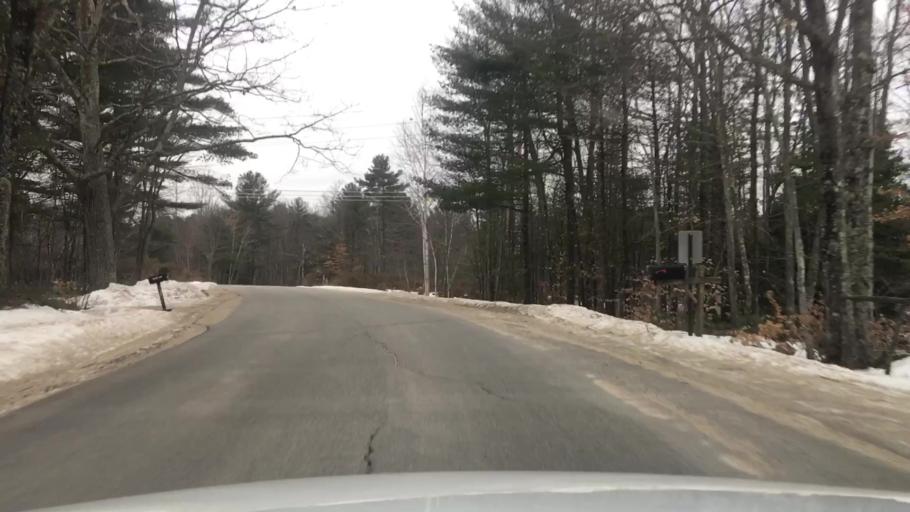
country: US
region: Maine
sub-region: York County
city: Shapleigh
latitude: 43.5032
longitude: -70.8223
